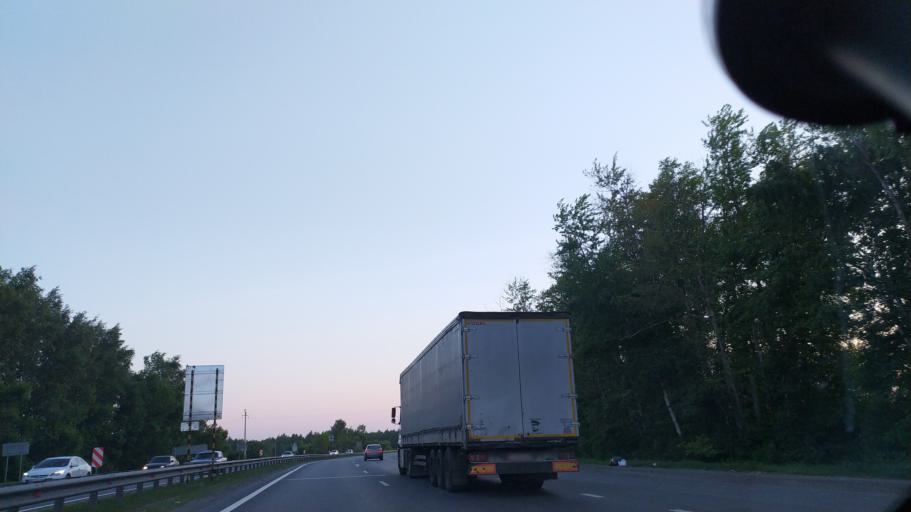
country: RU
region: Chuvashia
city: Ishley
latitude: 56.1009
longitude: 47.0328
